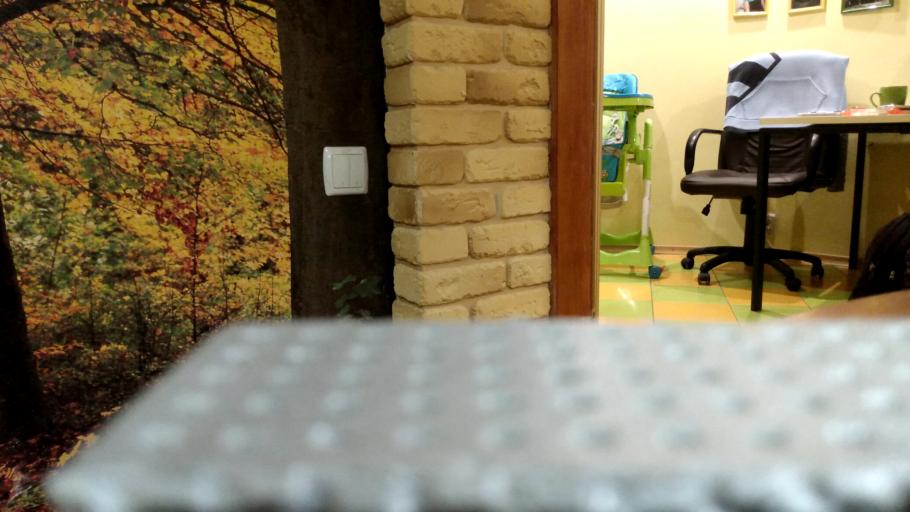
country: RU
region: Republic of Karelia
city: Pudozh
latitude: 61.9503
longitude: 37.6175
